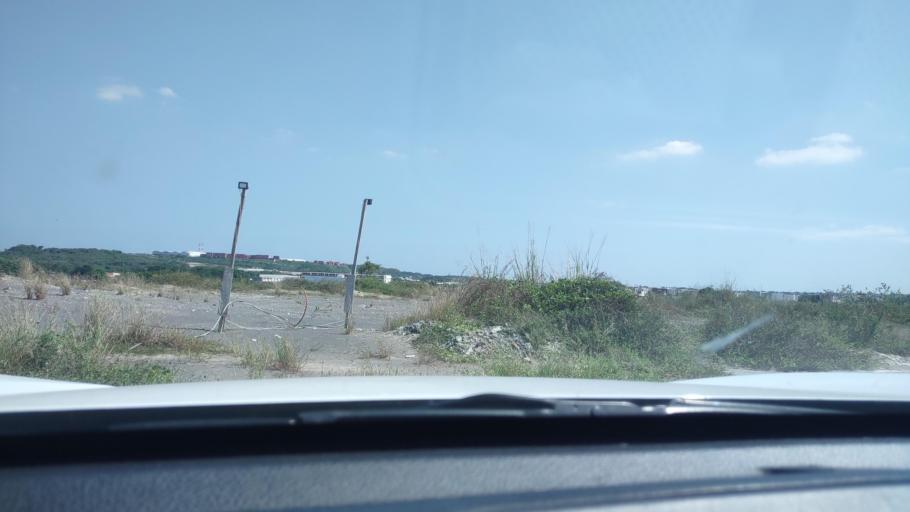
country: MX
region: Veracruz
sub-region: Veracruz
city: Fraccionamiento Geovillas los Pinos
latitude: 19.2208
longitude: -96.2341
